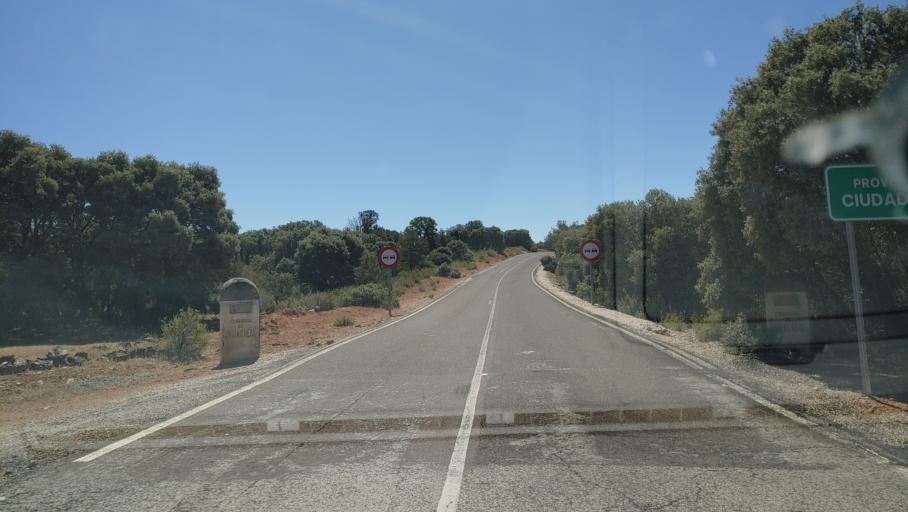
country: ES
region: Castille-La Mancha
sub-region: Provincia de Albacete
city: Ossa de Montiel
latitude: 38.8856
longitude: -2.7726
